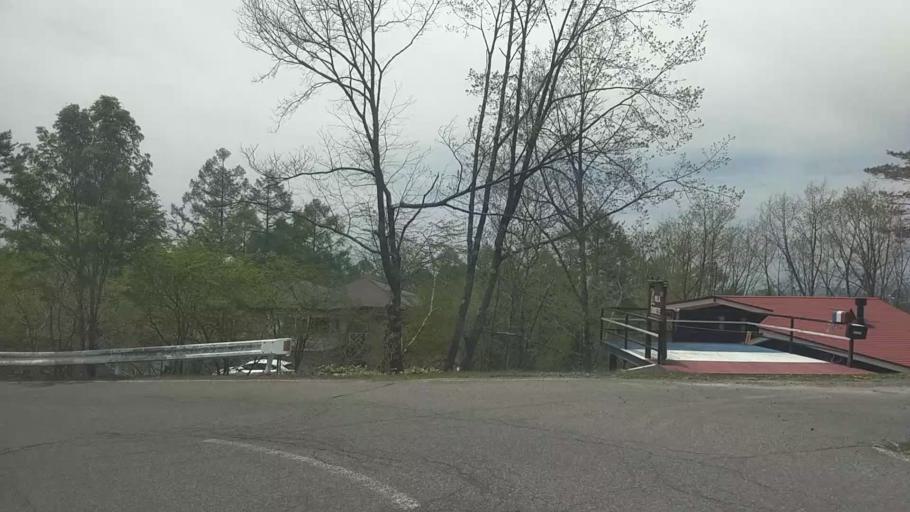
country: JP
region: Nagano
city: Chino
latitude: 36.0477
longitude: 138.3000
